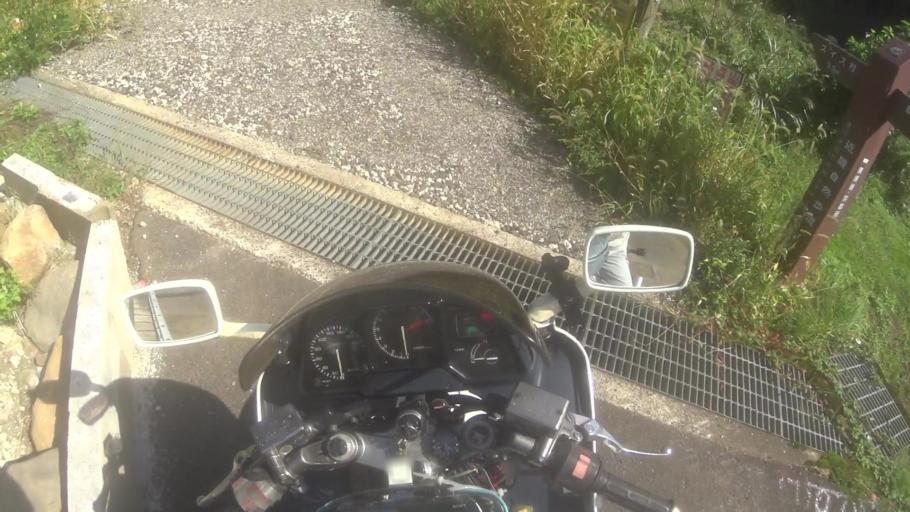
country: JP
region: Kyoto
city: Miyazu
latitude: 35.6817
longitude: 135.1698
